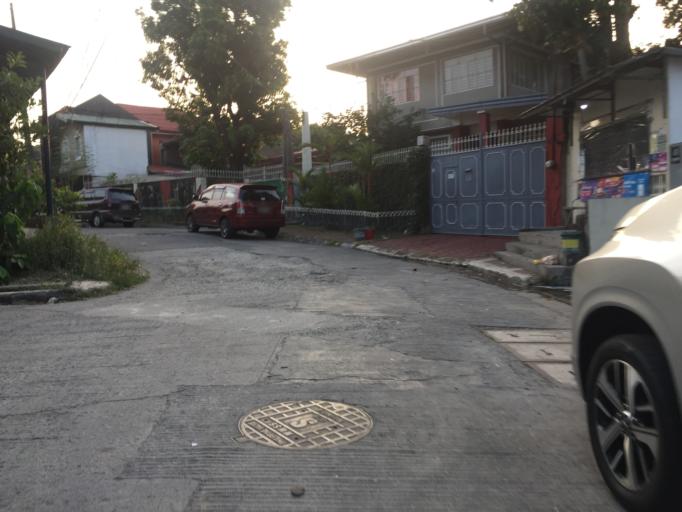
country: PH
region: Calabarzon
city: Bagong Pagasa
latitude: 14.6758
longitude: 121.0241
